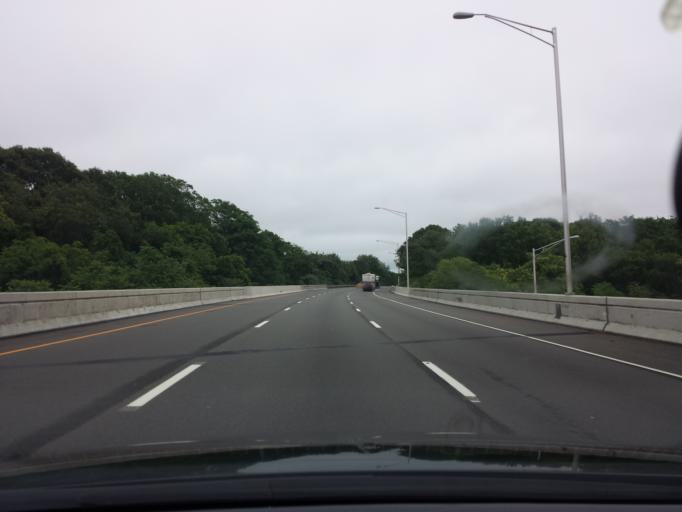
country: US
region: Connecticut
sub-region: New London County
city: Groton
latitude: 41.3643
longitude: -72.0678
